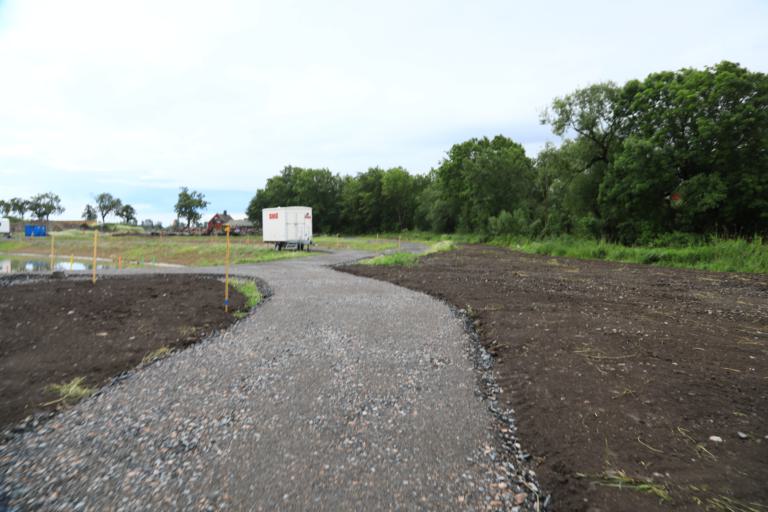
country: SE
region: Halland
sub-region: Varbergs Kommun
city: Varberg
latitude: 57.1374
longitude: 12.2730
